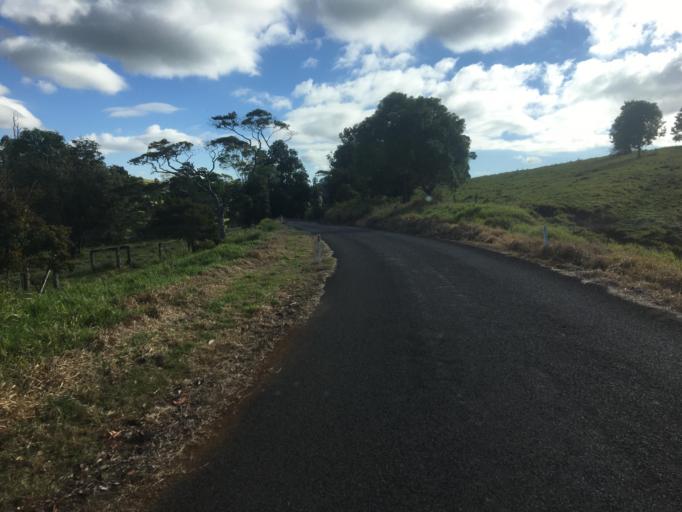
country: AU
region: Queensland
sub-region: Tablelands
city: Ravenshoe
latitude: -17.5859
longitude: 145.6036
